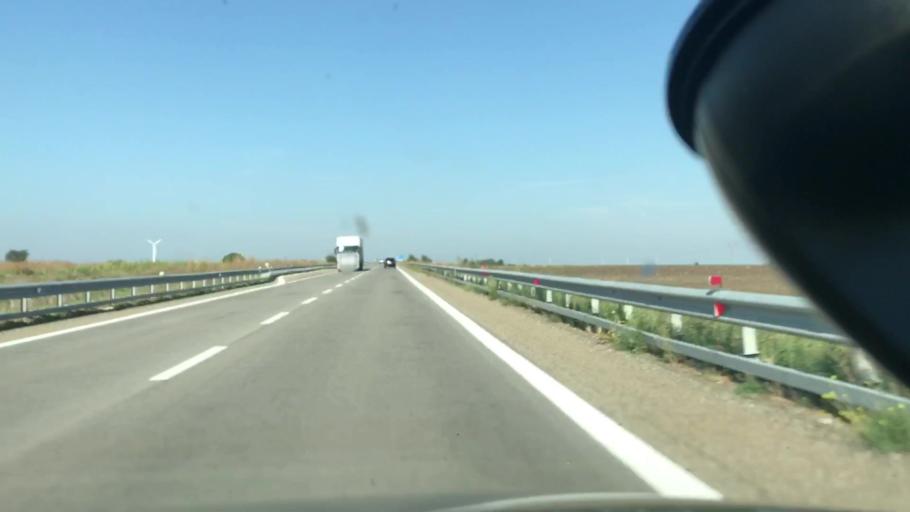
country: IT
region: Basilicate
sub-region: Provincia di Potenza
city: Montemilone
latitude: 40.9899
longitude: 15.9014
